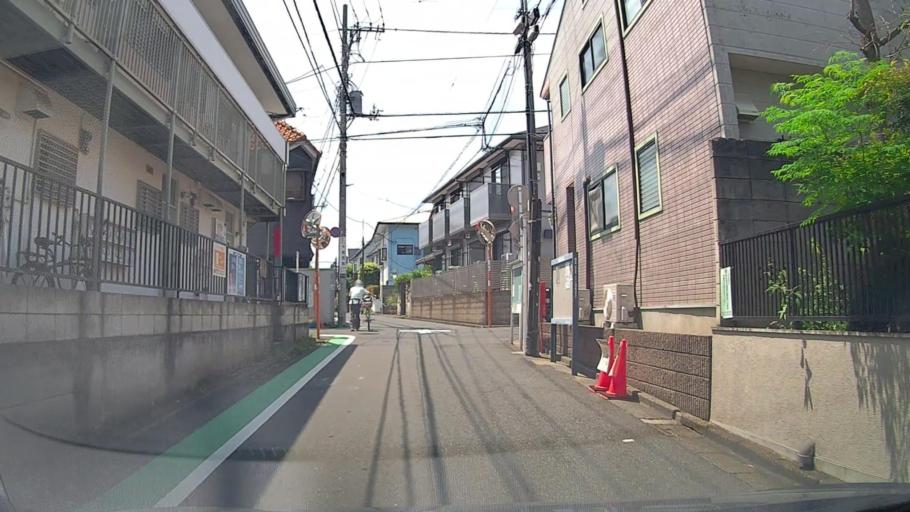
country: JP
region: Tokyo
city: Tokyo
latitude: 35.7154
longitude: 139.6408
